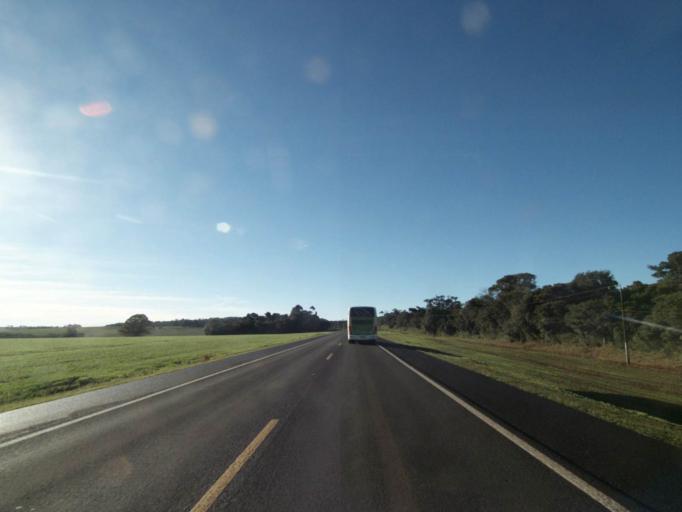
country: BR
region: Parana
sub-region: Matelandia
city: Matelandia
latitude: -25.1112
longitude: -53.7784
